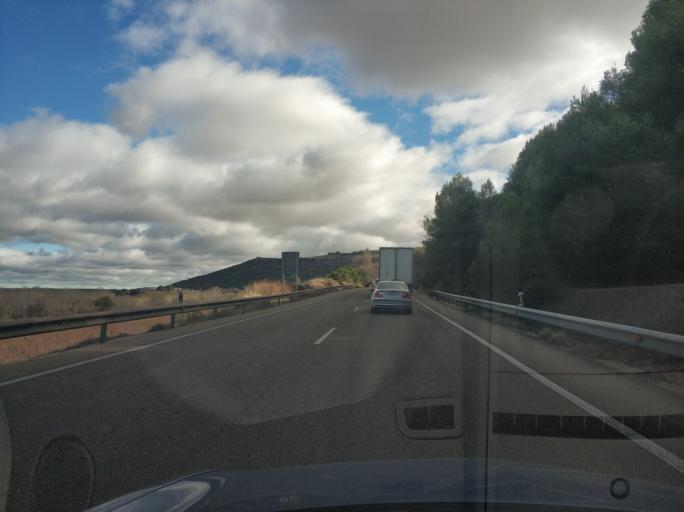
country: ES
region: Castille and Leon
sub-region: Provincia de Valladolid
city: Bocos de Duero
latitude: 41.6052
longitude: -4.0496
